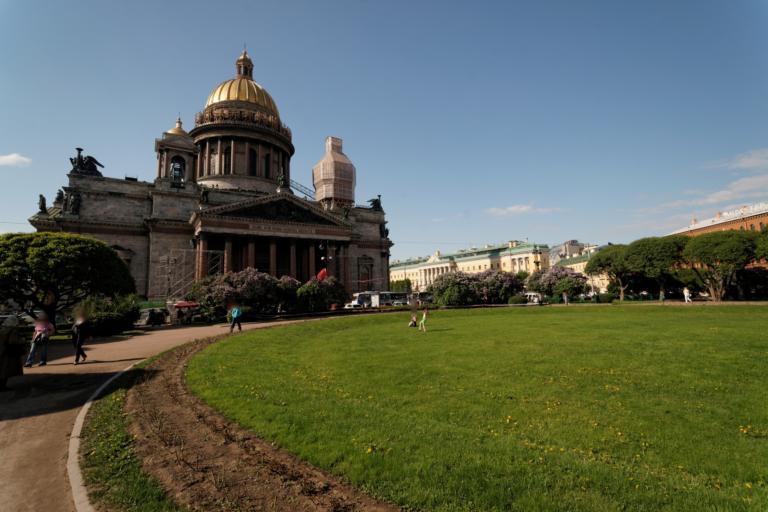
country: RU
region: St.-Petersburg
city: Saint Petersburg
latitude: 59.9329
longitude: 30.3072
